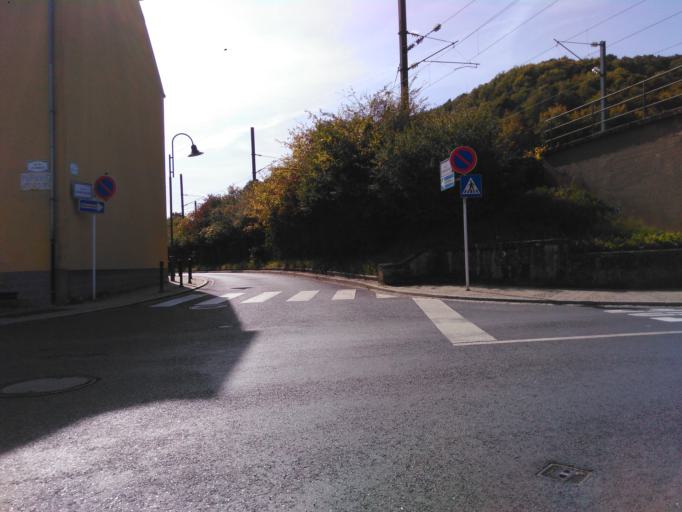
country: LU
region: Luxembourg
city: Tetange
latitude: 49.4746
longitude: 6.0345
